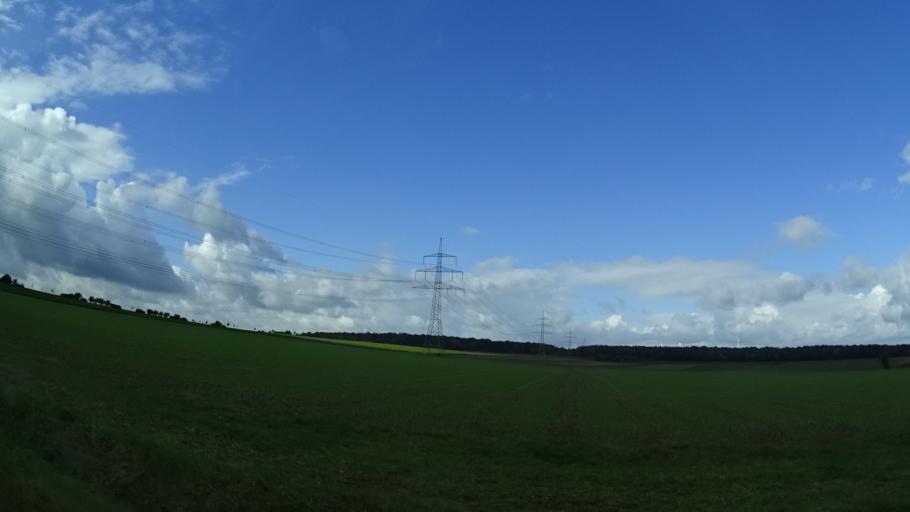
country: DE
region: Bavaria
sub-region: Regierungsbezirk Unterfranken
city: Lulsfeld
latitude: 49.8644
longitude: 10.3113
